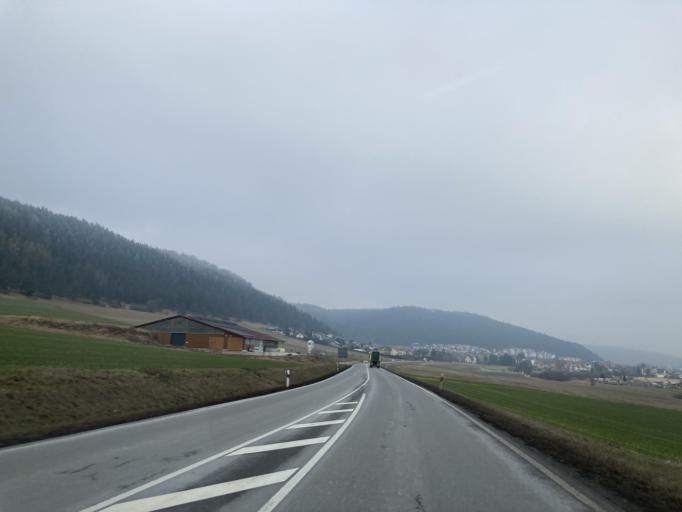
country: DE
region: Baden-Wuerttemberg
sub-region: Freiburg Region
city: Immendingen
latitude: 47.9306
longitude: 8.6975
